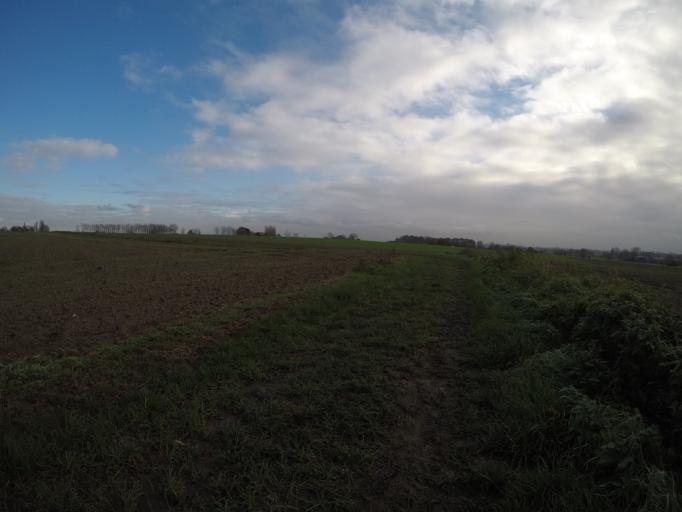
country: BE
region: Flanders
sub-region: Provincie West-Vlaanderen
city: Wervik
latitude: 50.8129
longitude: 3.0054
